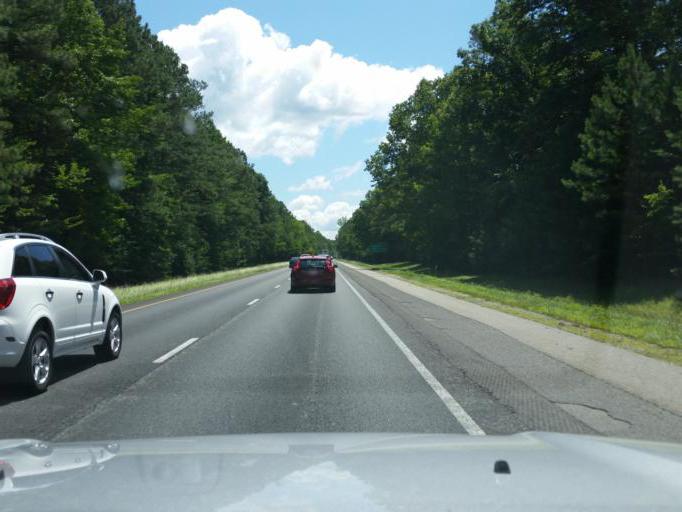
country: US
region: Virginia
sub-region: New Kent County
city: New Kent
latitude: 37.4830
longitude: -76.9396
